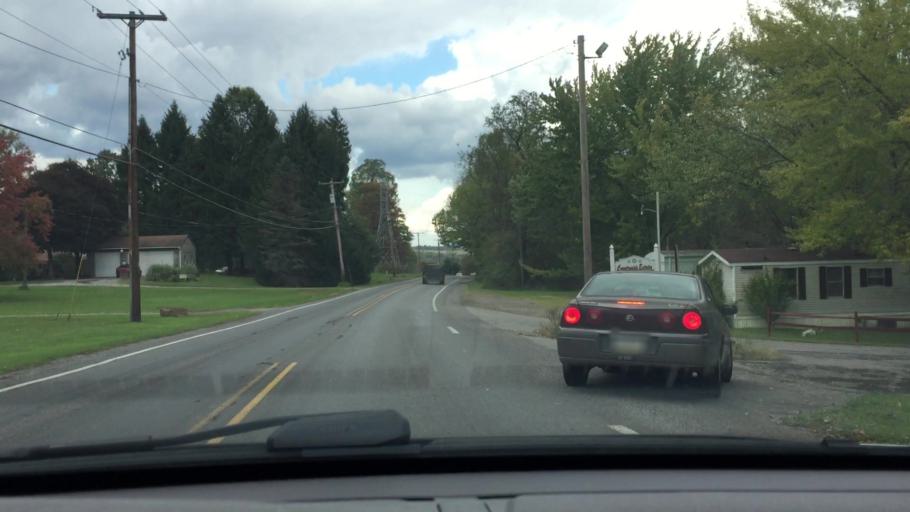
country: US
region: Pennsylvania
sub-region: Lawrence County
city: Oakwood
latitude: 41.0041
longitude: -80.4379
